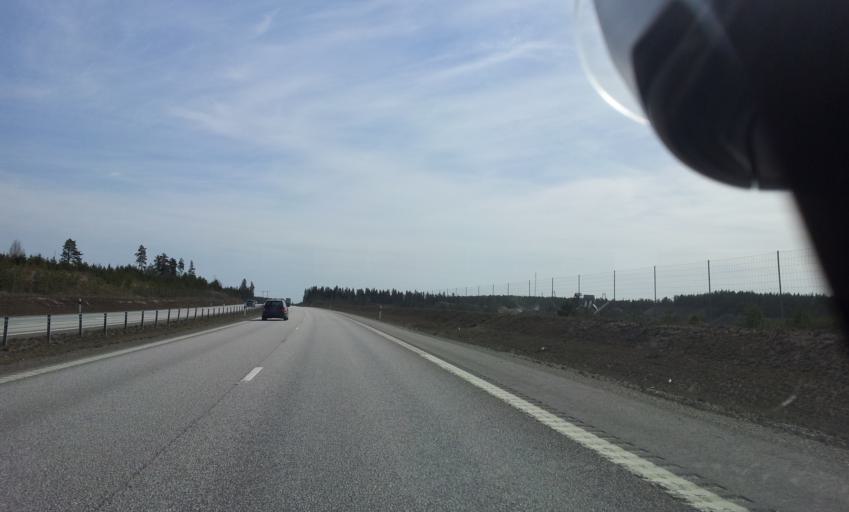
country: SE
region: Uppsala
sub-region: Osthammars Kommun
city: Bjorklinge
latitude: 60.1165
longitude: 17.5494
